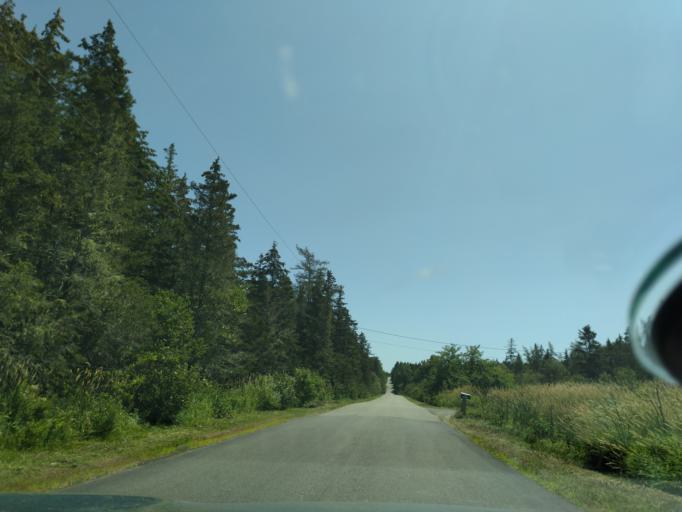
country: US
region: Maine
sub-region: Washington County
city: Eastport
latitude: 44.8373
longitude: -67.0119
